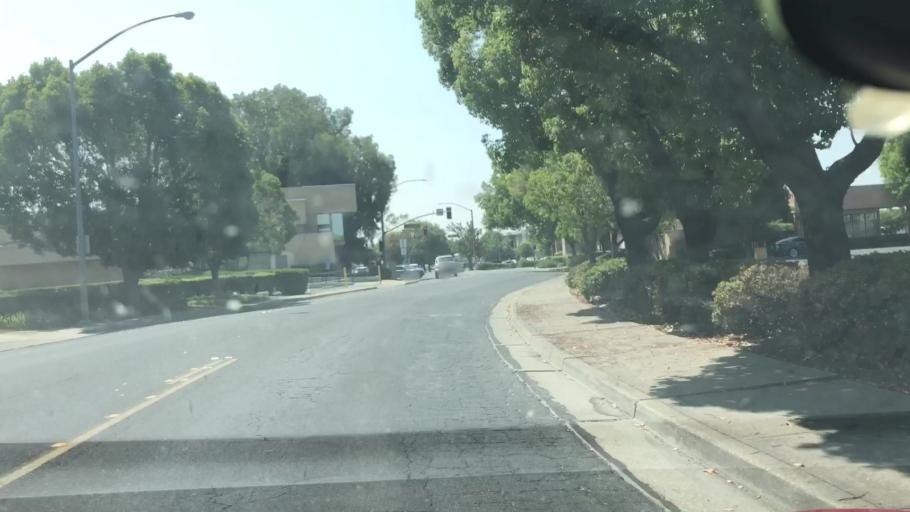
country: US
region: California
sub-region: San Joaquin County
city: Lincoln Village
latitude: 37.9987
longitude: -121.3103
